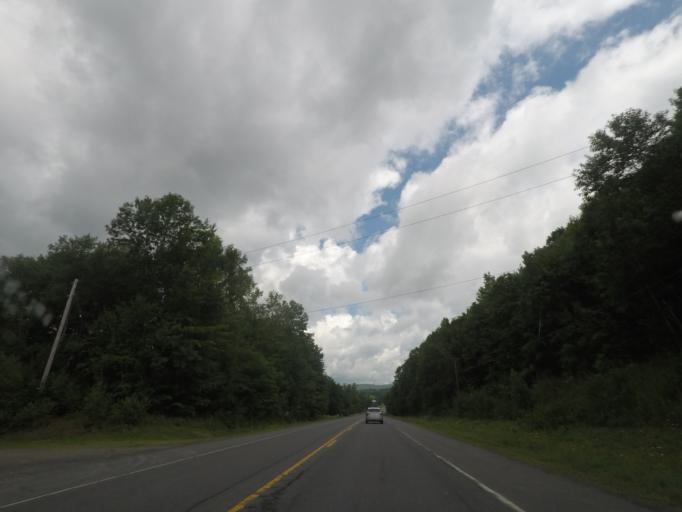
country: US
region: Massachusetts
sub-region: Berkshire County
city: Lanesborough
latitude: 42.5879
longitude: -73.3676
